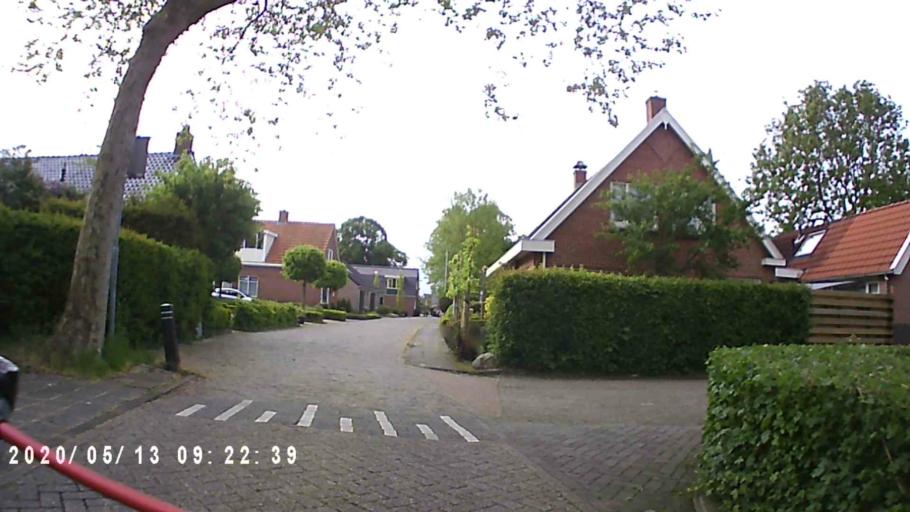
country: NL
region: Groningen
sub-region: Gemeente Zuidhorn
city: Noordhorn
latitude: 53.2620
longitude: 6.3961
